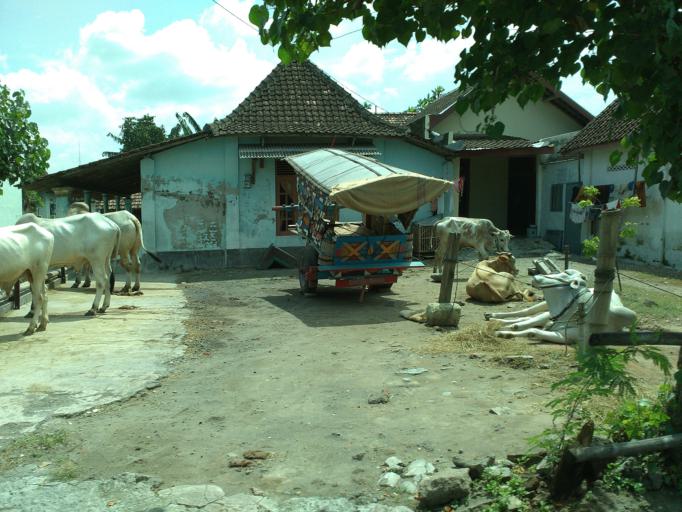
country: ID
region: Central Java
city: Kebonarun
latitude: -7.7167
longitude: 110.5781
